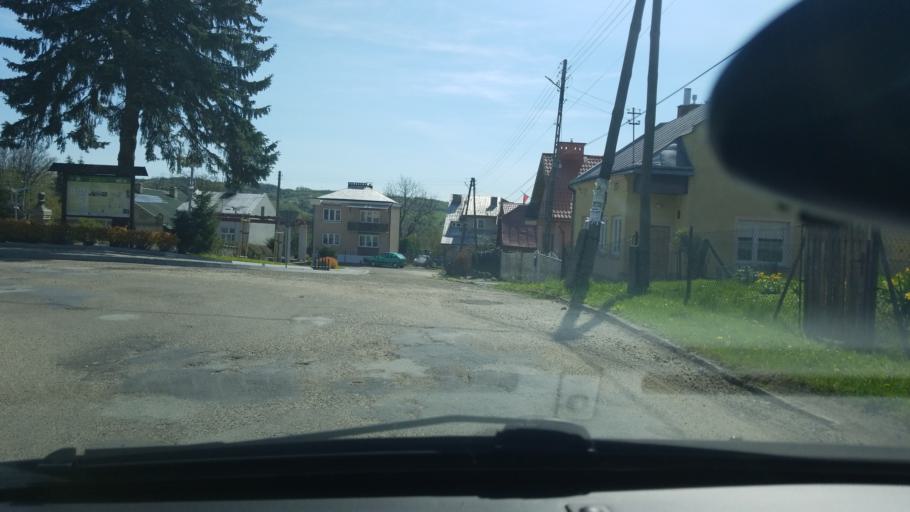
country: PL
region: Subcarpathian Voivodeship
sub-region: Powiat jasielski
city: Debowiec
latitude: 49.6823
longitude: 21.4636
